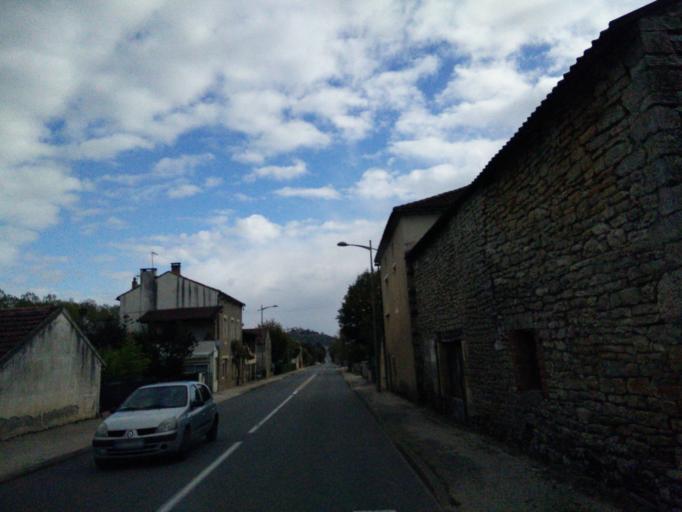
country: FR
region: Midi-Pyrenees
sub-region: Departement du Lot
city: Pradines
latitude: 44.5107
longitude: 1.3723
